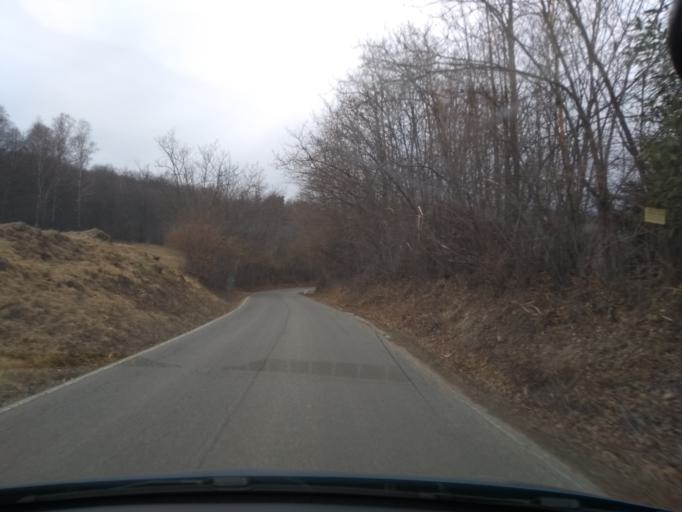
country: IT
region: Piedmont
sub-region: Provincia di Biella
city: Zubiena
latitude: 45.4882
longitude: 7.9895
